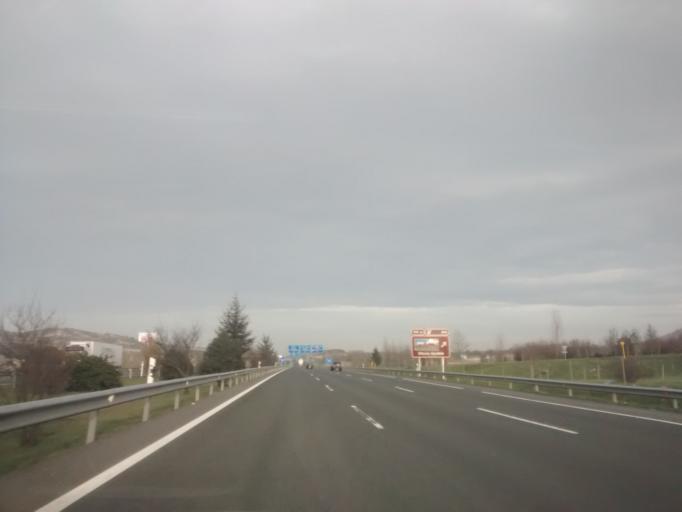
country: ES
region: Basque Country
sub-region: Provincia de Alava
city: Gasteiz / Vitoria
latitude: 42.8204
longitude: -2.7765
